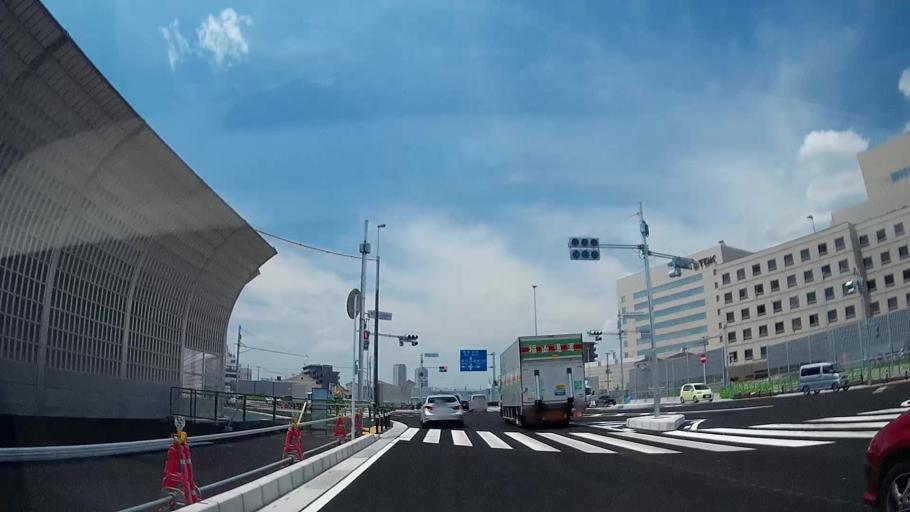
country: JP
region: Tokyo
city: Urayasu
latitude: 35.7128
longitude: 139.9219
